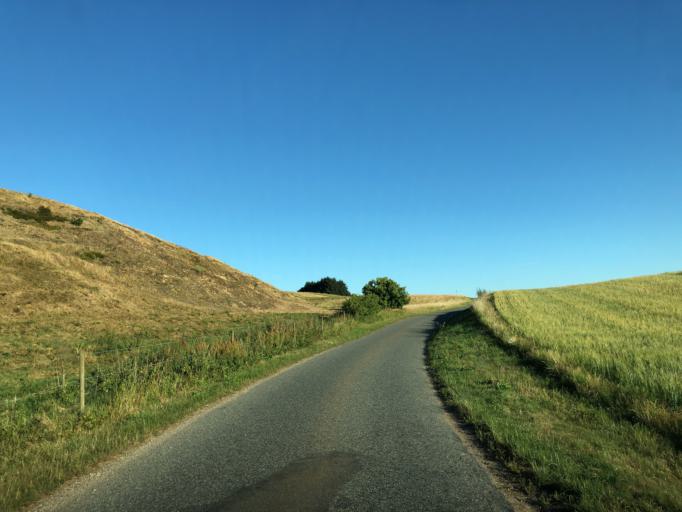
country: DK
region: Central Jutland
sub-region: Skanderborg Kommune
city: Ry
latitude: 55.9850
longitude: 9.7929
